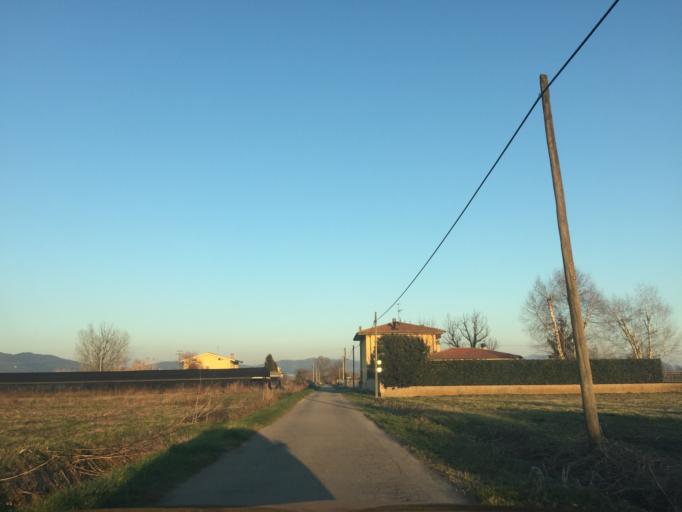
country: IT
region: Tuscany
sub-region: Provincia di Pistoia
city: Anchione
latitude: 43.8276
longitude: 10.7691
